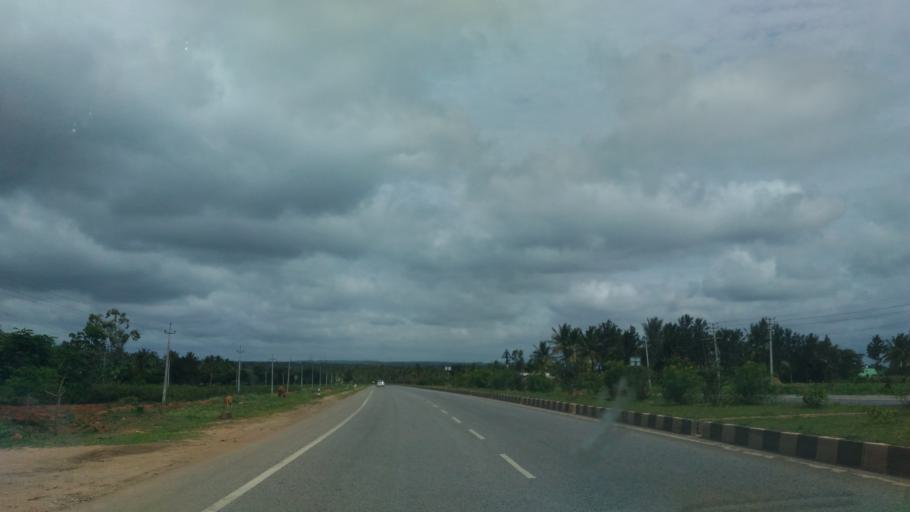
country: IN
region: Karnataka
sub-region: Hassan
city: Channarayapatna
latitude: 12.9763
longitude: 76.2554
